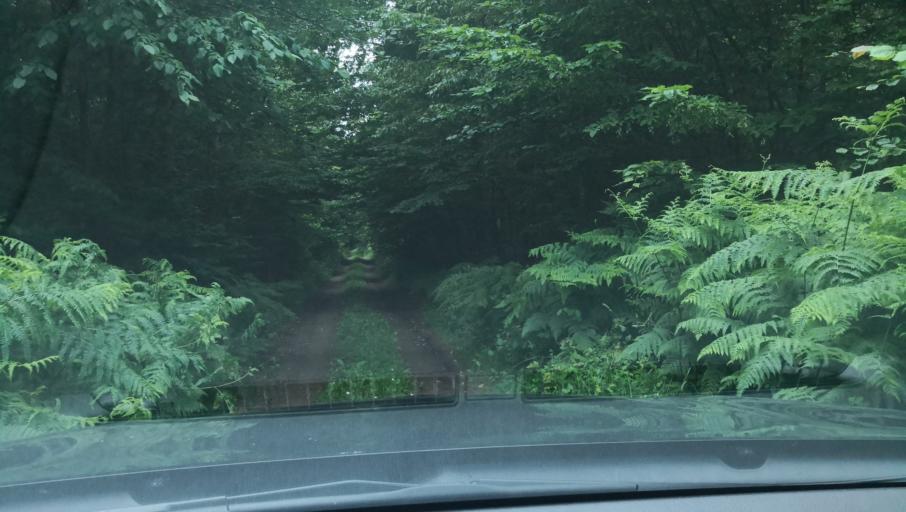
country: SE
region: Skane
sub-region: Simrishamns Kommun
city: Kivik
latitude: 55.6180
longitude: 14.1084
